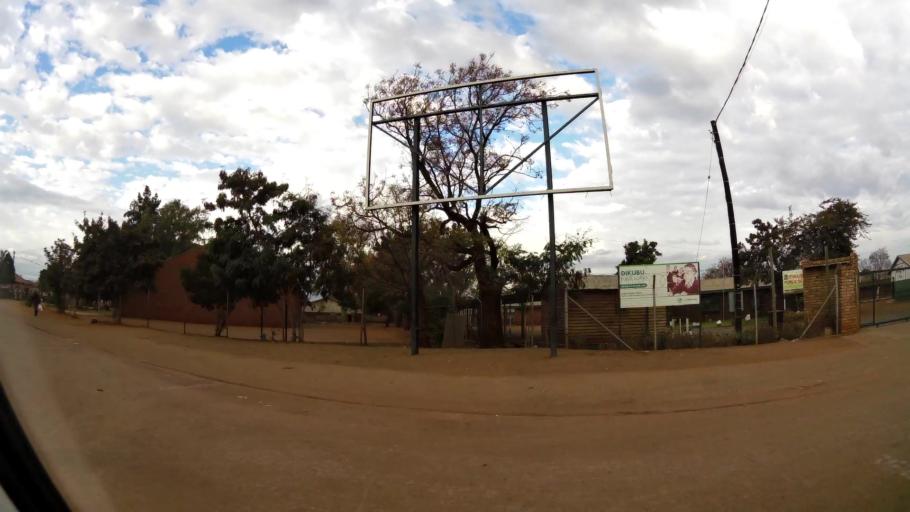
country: ZA
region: Limpopo
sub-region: Waterberg District Municipality
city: Modimolle
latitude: -24.5221
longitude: 28.7234
